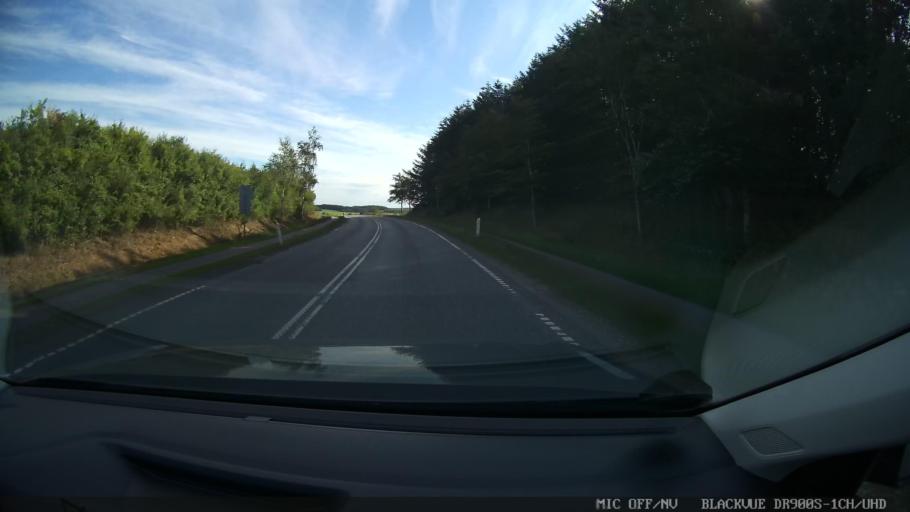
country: DK
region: North Denmark
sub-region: Mariagerfjord Kommune
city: Arden
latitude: 56.7724
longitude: 9.8221
